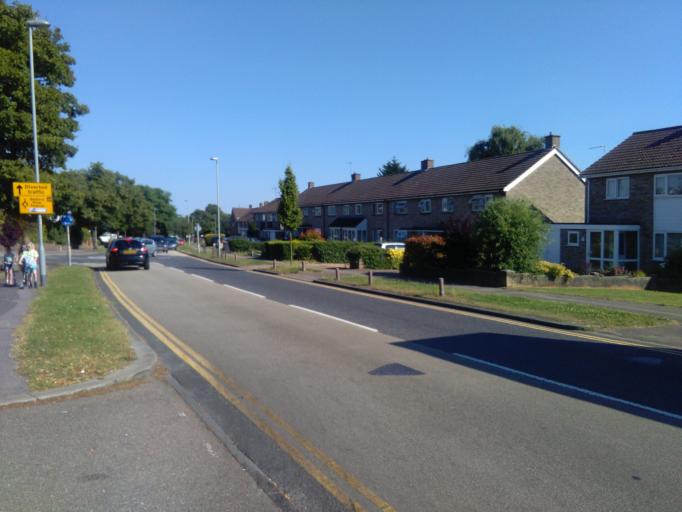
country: GB
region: England
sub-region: Bedford
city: Bedford
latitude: 52.1538
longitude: -0.4642
